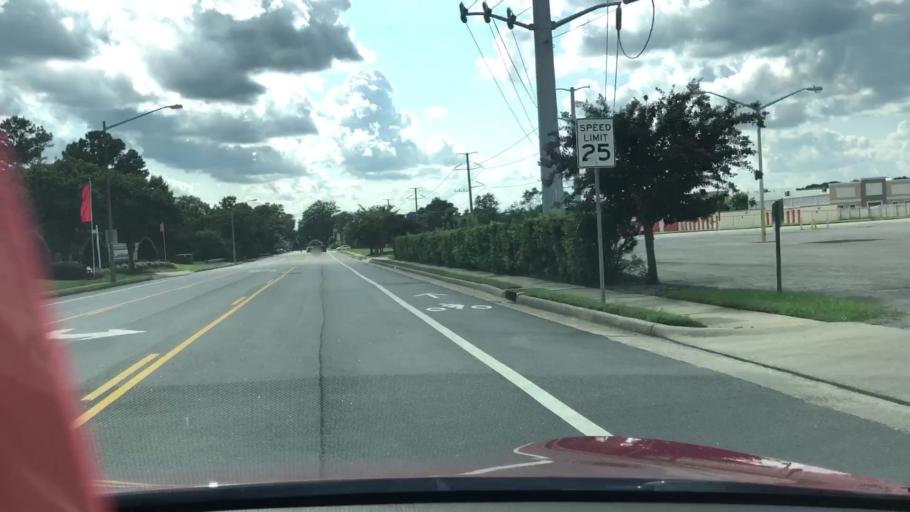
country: US
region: Virginia
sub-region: City of Virginia Beach
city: Virginia Beach
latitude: 36.8478
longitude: -76.0252
